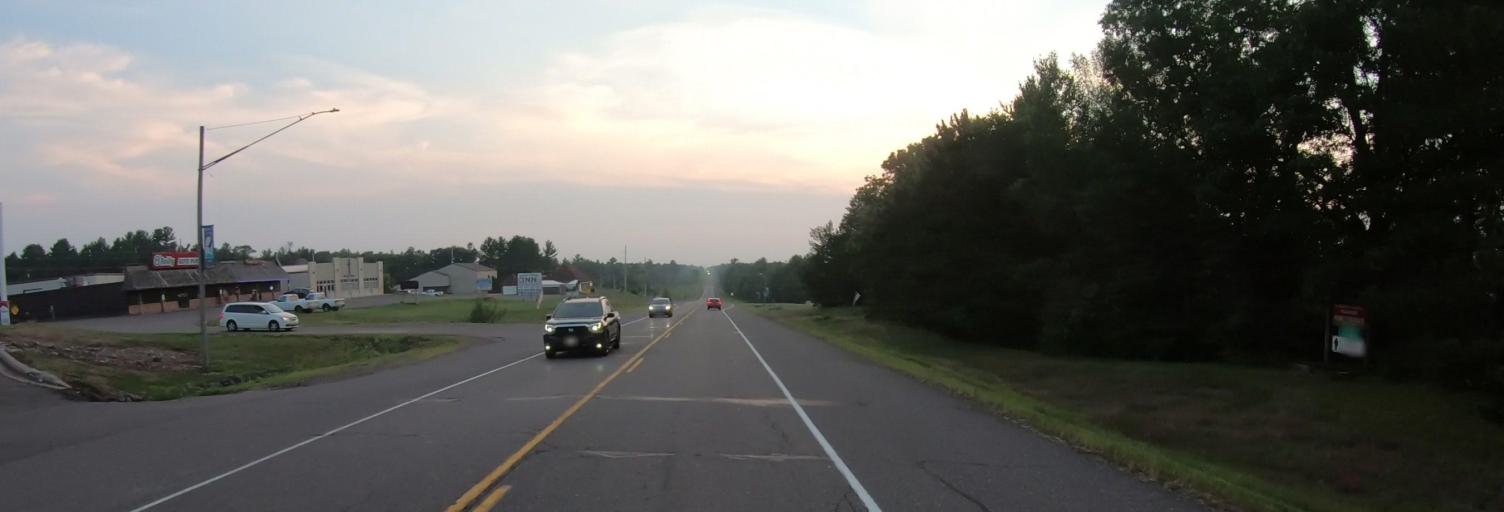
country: US
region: Wisconsin
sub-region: Burnett County
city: Grantsburg
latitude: 45.7730
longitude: -92.6971
